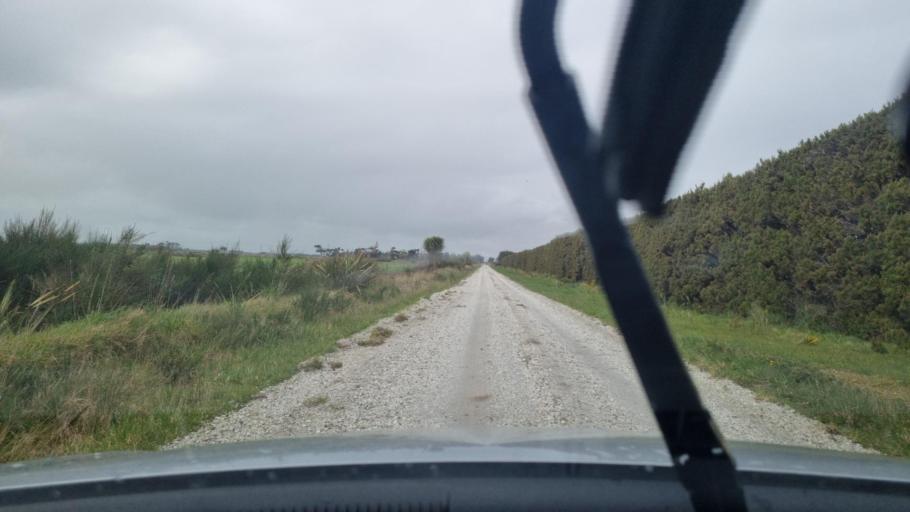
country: NZ
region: Southland
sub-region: Invercargill City
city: Invercargill
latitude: -46.4987
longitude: 168.4134
